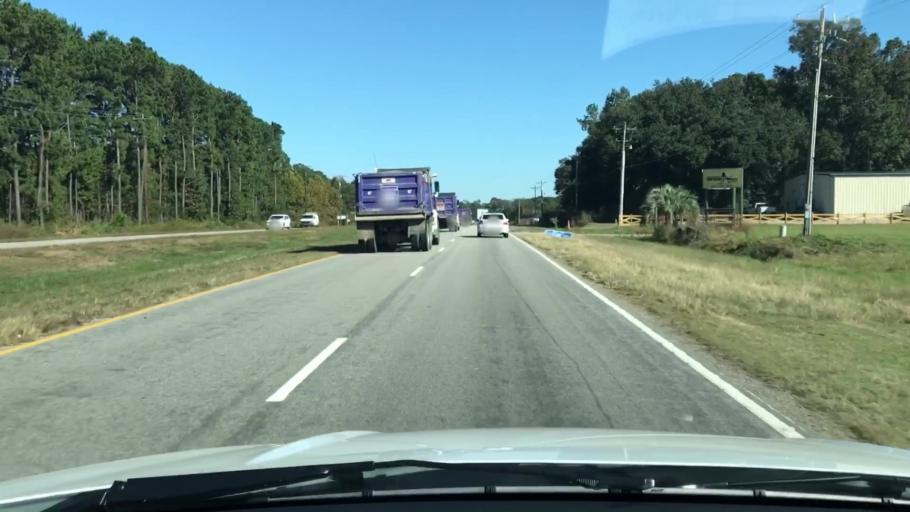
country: US
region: South Carolina
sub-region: Charleston County
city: Shell Point
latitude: 32.7809
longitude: -80.1603
